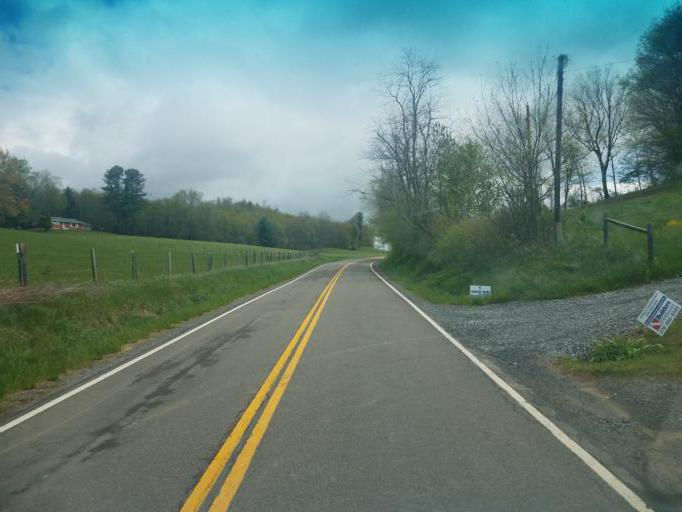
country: US
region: Virginia
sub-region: Wythe County
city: Rural Retreat
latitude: 37.0060
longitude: -81.3682
